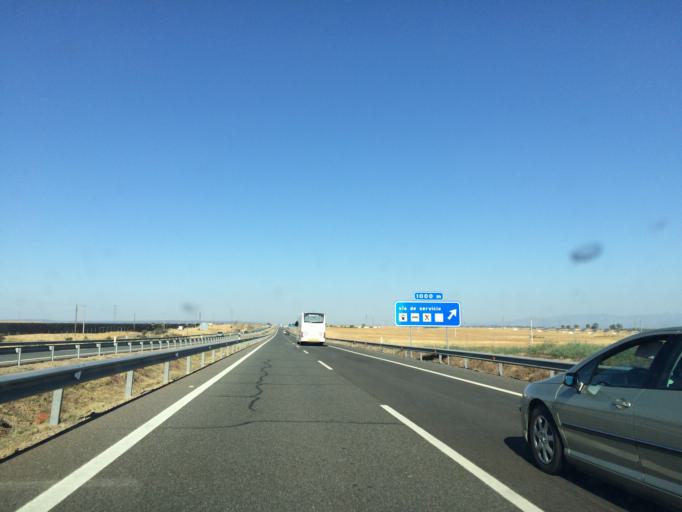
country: ES
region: Castille-La Mancha
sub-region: Province of Toledo
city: Caleruela
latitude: 39.8952
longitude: -5.3139
